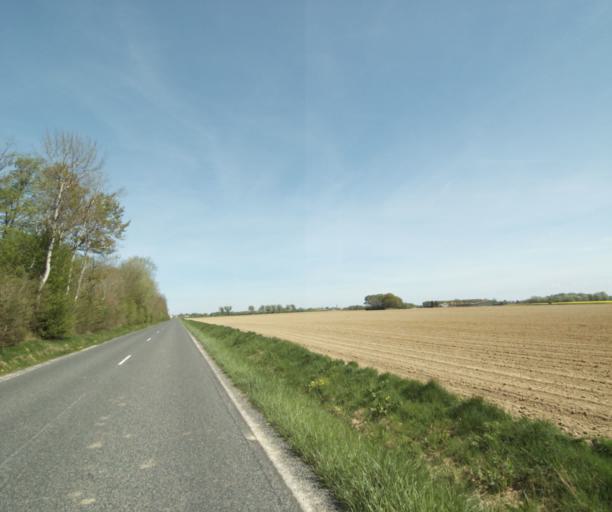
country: FR
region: Ile-de-France
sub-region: Departement de Seine-et-Marne
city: Nangis
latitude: 48.5405
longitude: 2.9904
